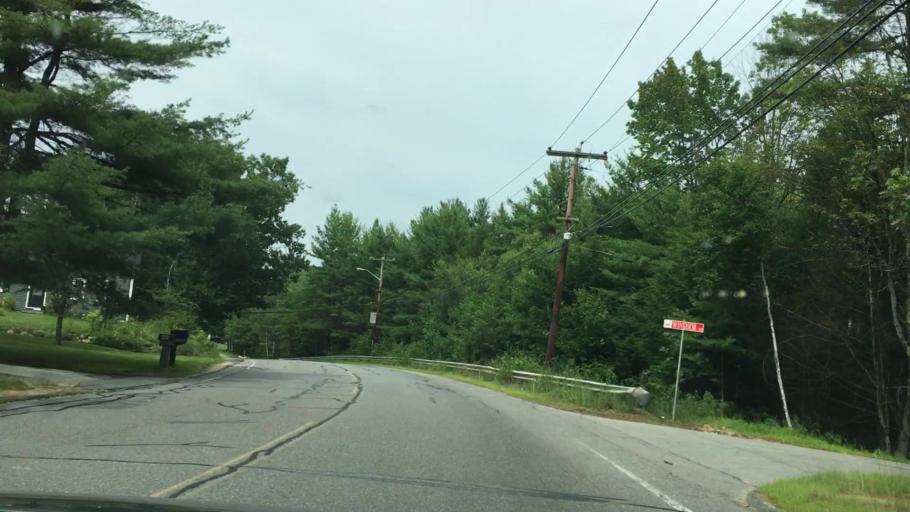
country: US
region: Massachusetts
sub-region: Worcester County
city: Winchendon
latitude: 42.6866
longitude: -72.0156
